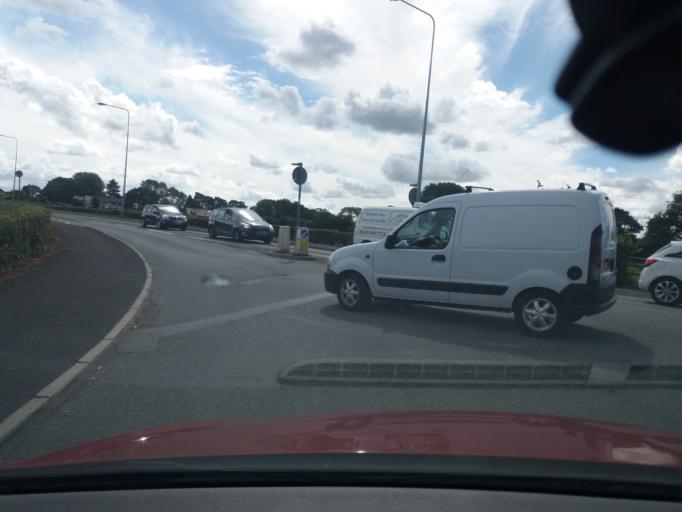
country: GB
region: England
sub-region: Lancashire
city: Coppull
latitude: 53.6293
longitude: -2.6855
